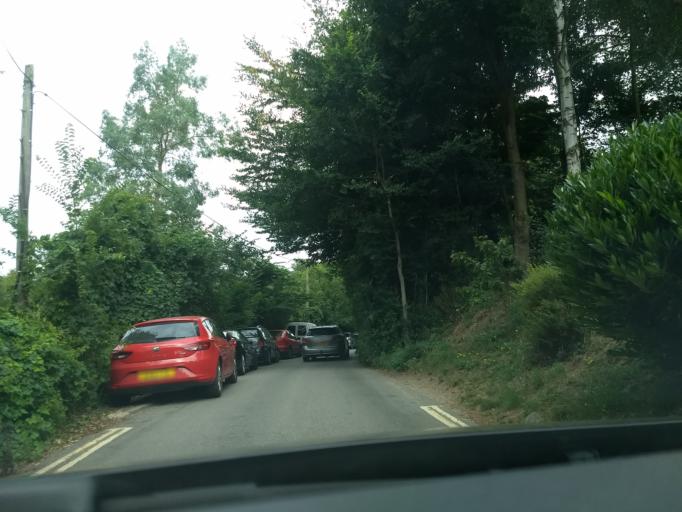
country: GB
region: England
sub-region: Suffolk
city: Shotley Gate
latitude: 51.9939
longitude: 1.2124
